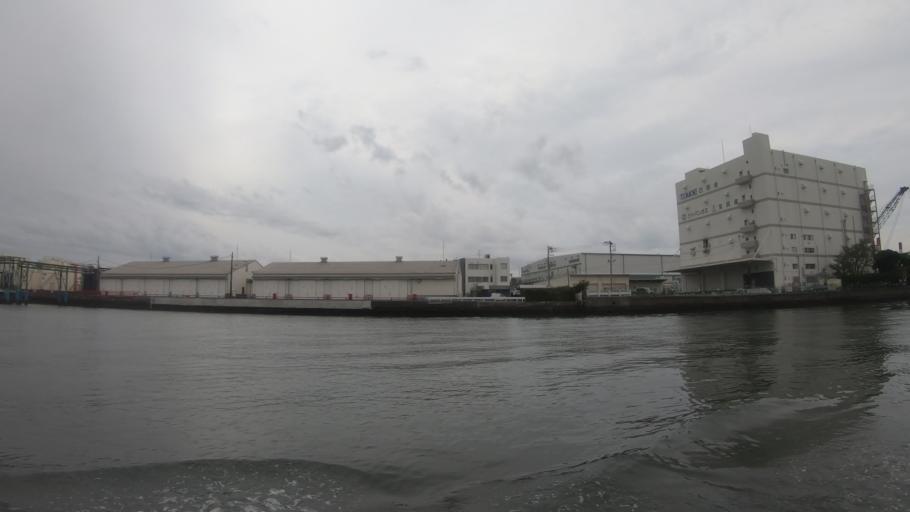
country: JP
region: Kanagawa
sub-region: Kawasaki-shi
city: Kawasaki
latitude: 35.4905
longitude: 139.6781
